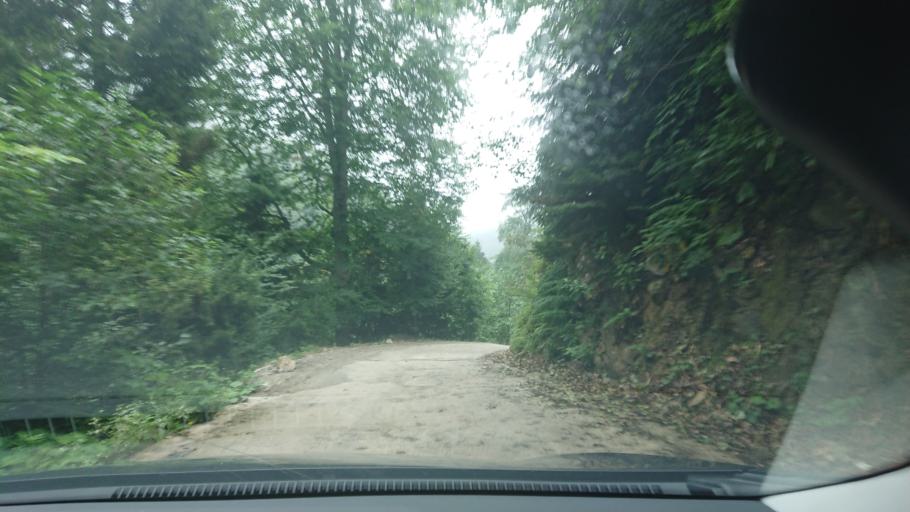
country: TR
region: Gumushane
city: Kurtun
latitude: 40.6631
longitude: 39.0298
